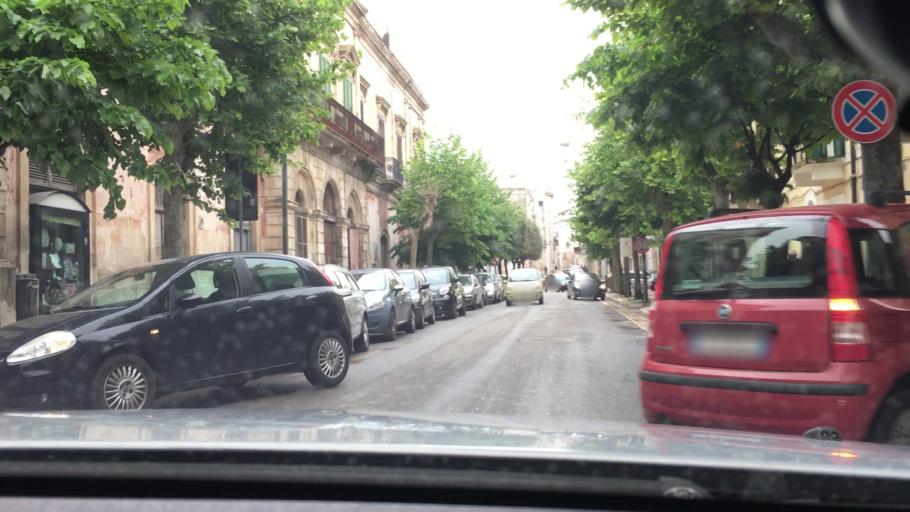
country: IT
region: Apulia
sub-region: Provincia di Bari
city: Gioia del Colle
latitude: 40.8023
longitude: 16.9231
